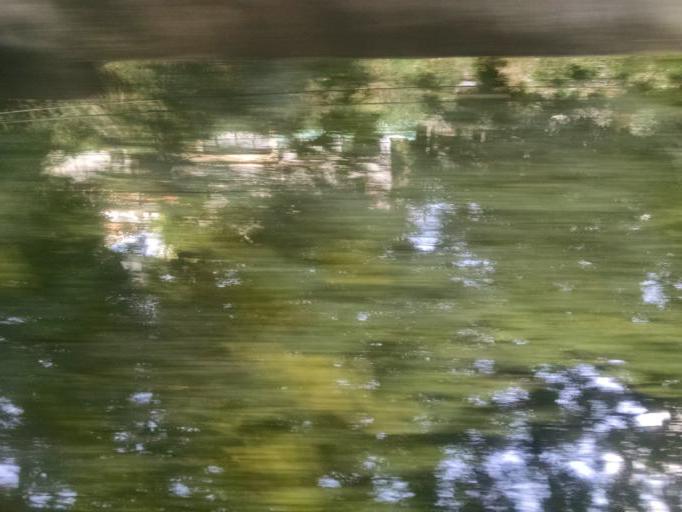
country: BR
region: Rio de Janeiro
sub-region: Rio De Janeiro
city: Rio de Janeiro
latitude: -22.8723
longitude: -43.2880
